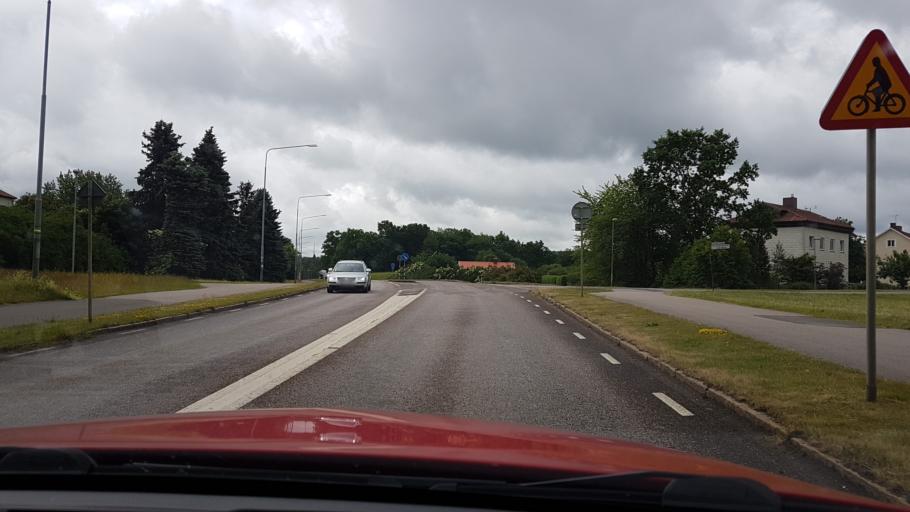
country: SE
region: Vaestra Goetaland
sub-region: Skovde Kommun
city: Skoevde
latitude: 58.3814
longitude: 13.8374
